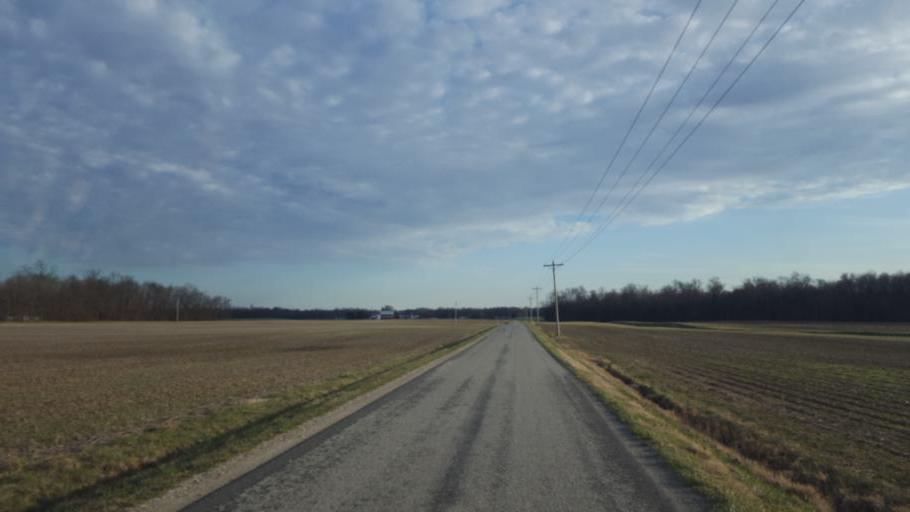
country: US
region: Ohio
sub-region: Marion County
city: Marion
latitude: 40.6112
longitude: -82.9910
